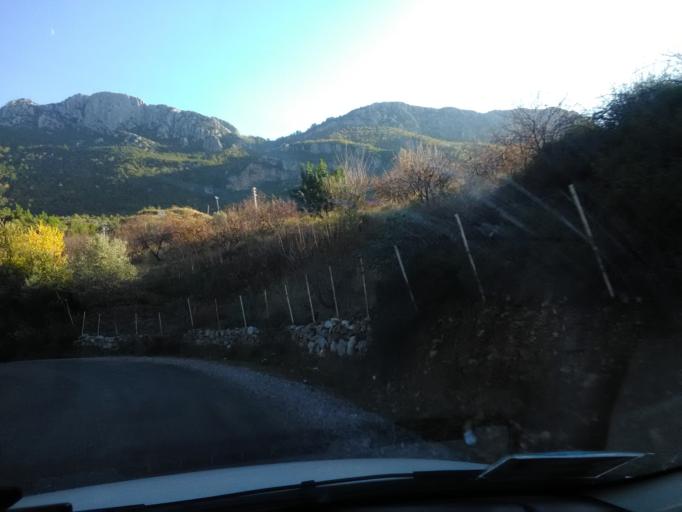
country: TR
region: Antalya
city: Gazipasa
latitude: 36.3117
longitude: 32.4091
